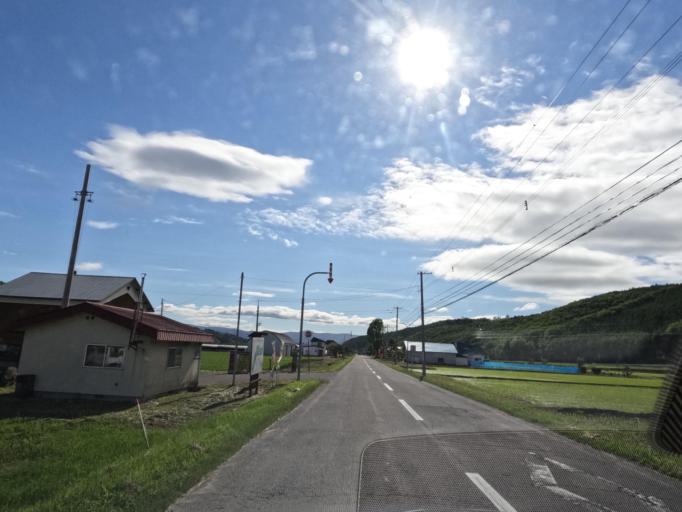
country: JP
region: Hokkaido
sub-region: Asahikawa-shi
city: Asahikawa
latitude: 43.6261
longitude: 142.5122
